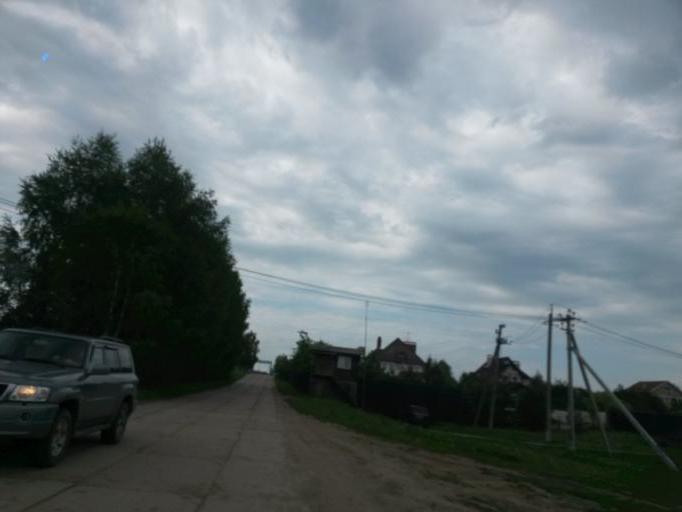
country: RU
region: Moskovskaya
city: Melikhovo
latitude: 55.1527
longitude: 37.6306
